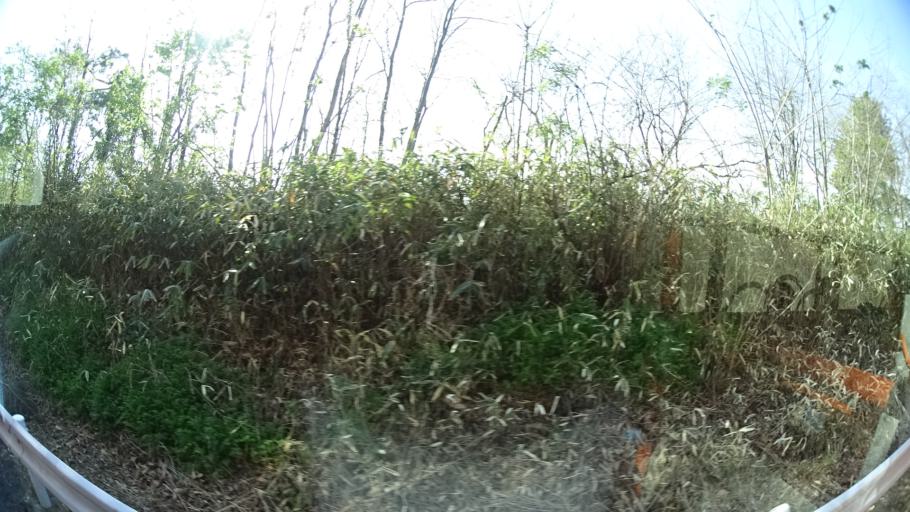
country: JP
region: Iwate
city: Ofunato
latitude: 39.0033
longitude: 141.7119
